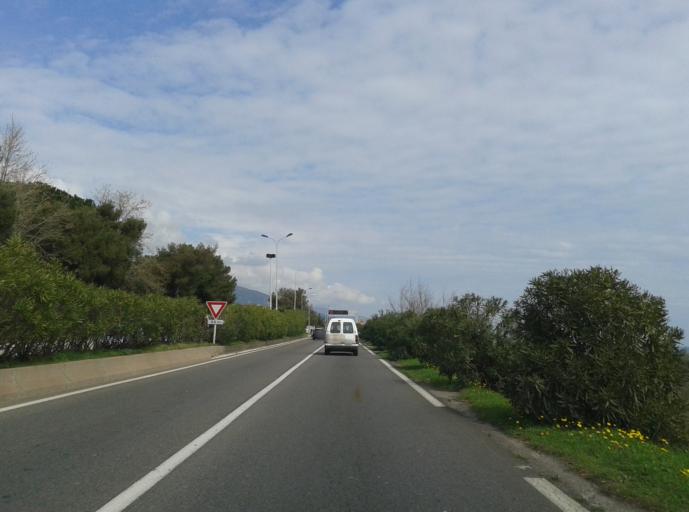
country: FR
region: Corsica
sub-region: Departement de la Haute-Corse
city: Furiani
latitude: 42.6697
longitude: 9.4433
